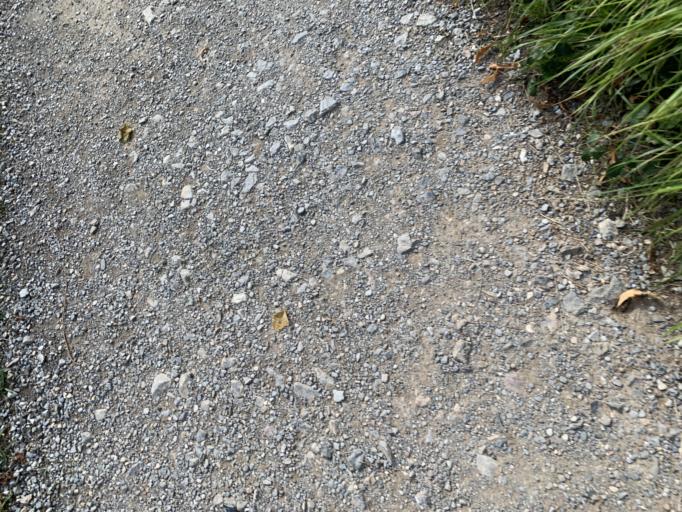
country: ES
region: Castille and Leon
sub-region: Provincia de Leon
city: Posada de Valdeon
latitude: 43.2291
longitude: -4.8941
